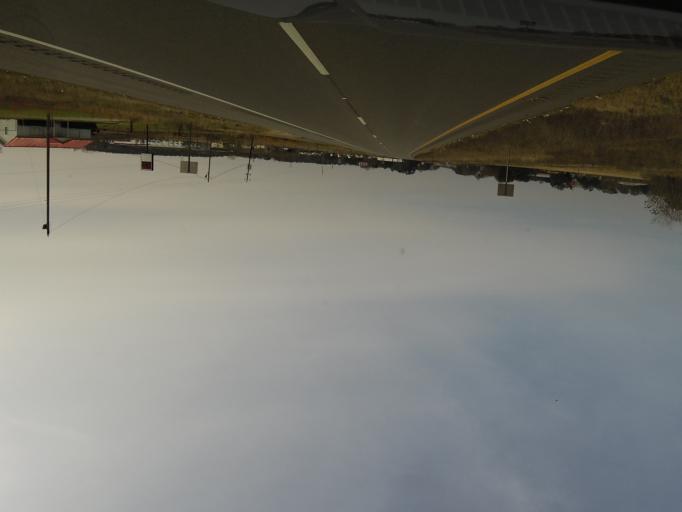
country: US
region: Alabama
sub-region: Houston County
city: Ashford
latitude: 31.1737
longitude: -85.2324
